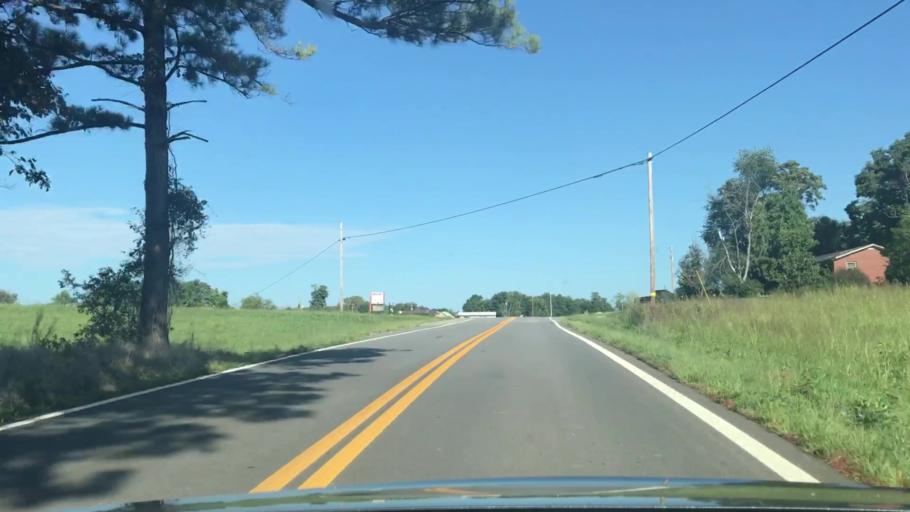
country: US
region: Tennessee
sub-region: Pickett County
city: Byrdstown
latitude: 36.6202
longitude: -85.0829
